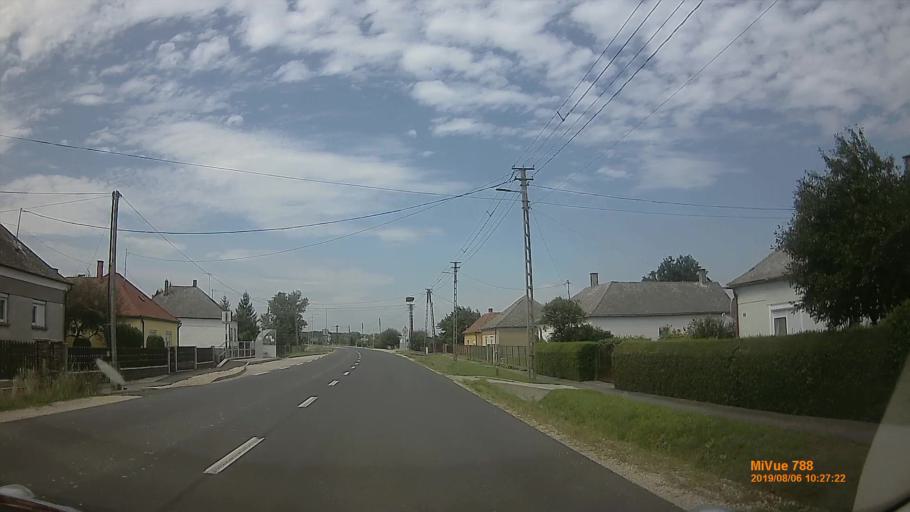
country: HU
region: Vas
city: Kormend
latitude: 47.0436
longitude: 16.6698
